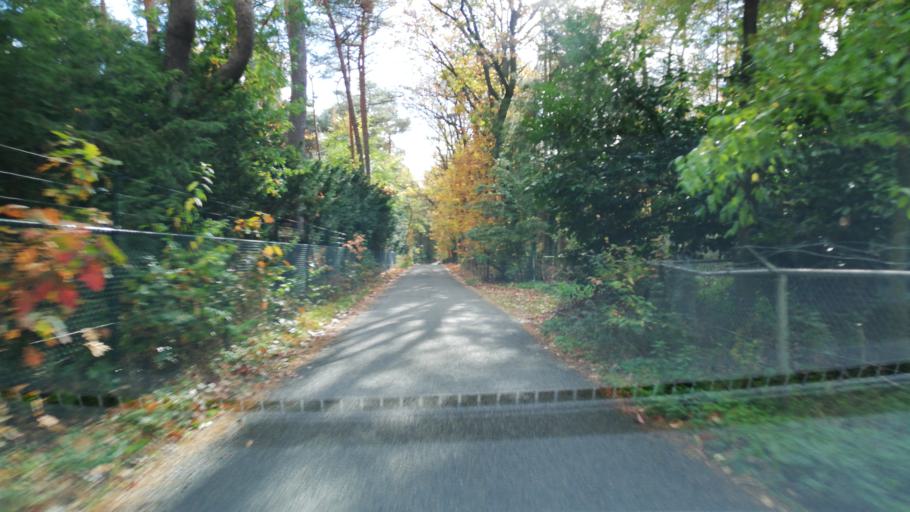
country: NL
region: Gelderland
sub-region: Gemeente Apeldoorn
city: Beekbergen
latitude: 52.1415
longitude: 5.9684
